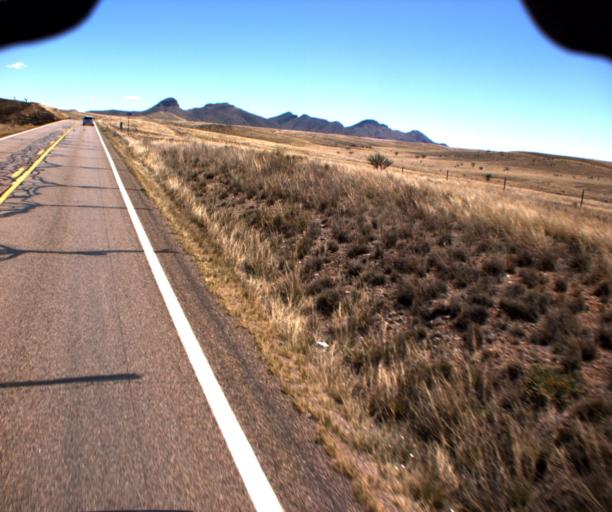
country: US
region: Arizona
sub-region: Cochise County
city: Huachuca City
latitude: 31.7104
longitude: -110.5701
